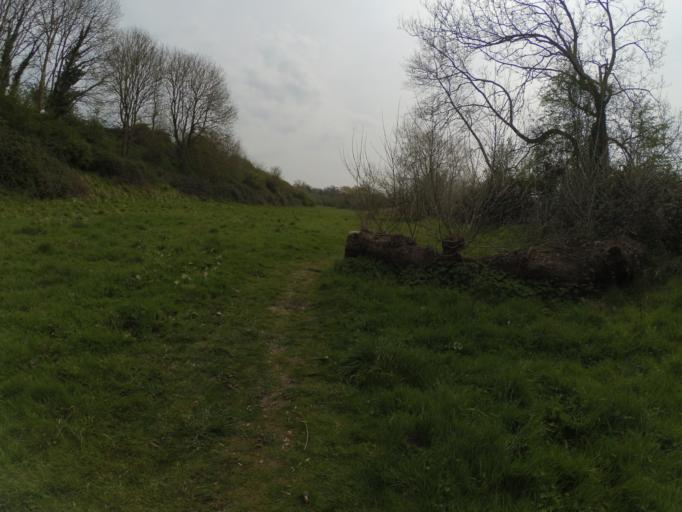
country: GB
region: England
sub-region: West Sussex
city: Arundel
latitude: 50.8728
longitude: -0.5305
